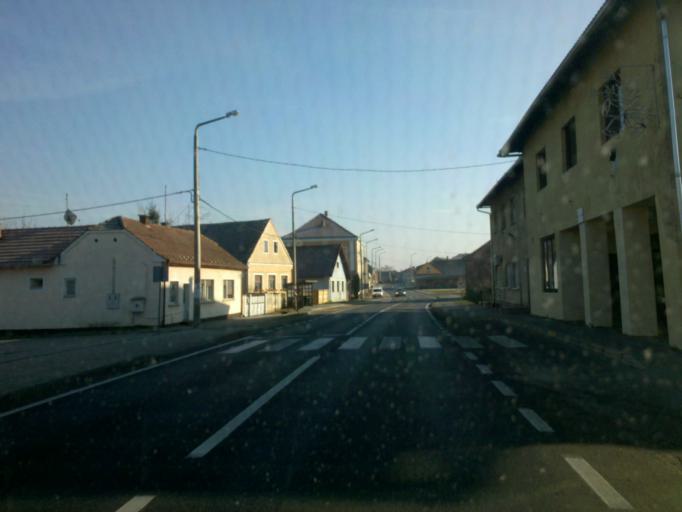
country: HR
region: Koprivnicko-Krizevacka
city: Virje
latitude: 46.0754
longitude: 16.9503
